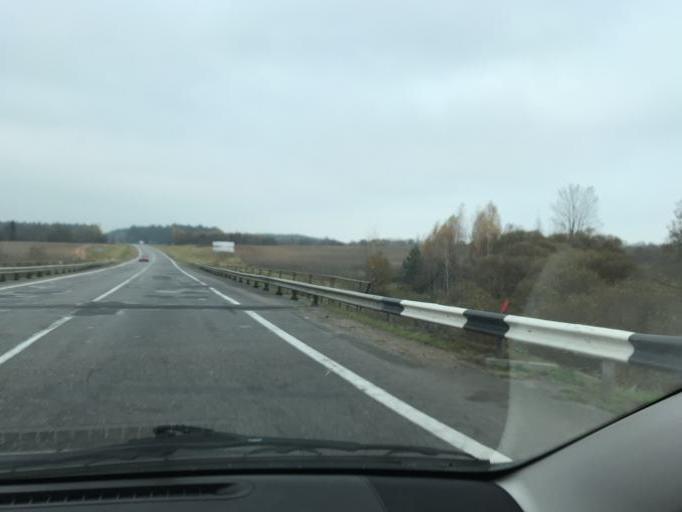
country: BY
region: Vitebsk
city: Syanno
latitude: 55.0453
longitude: 29.5155
